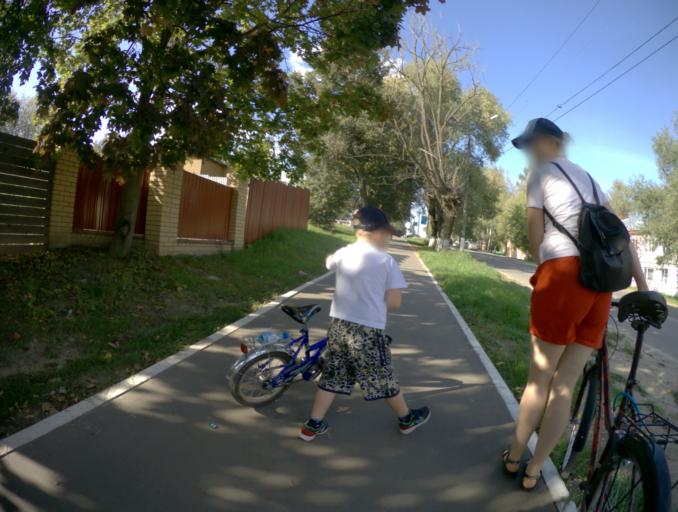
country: RU
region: Vladimir
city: Petushki
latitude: 55.9300
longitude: 39.4573
